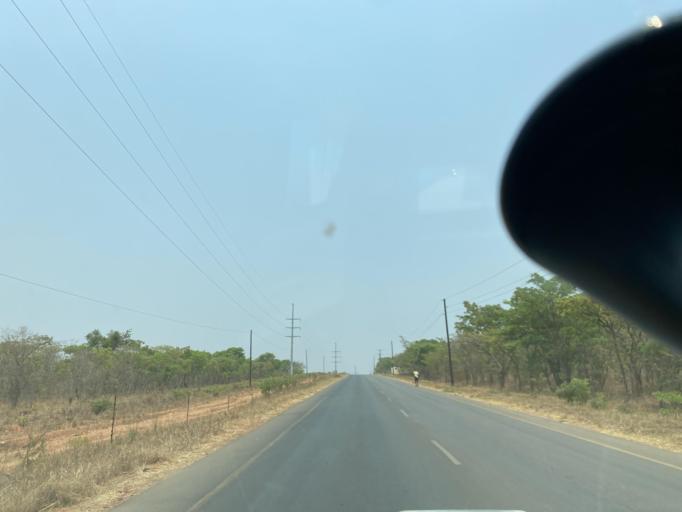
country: ZM
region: Lusaka
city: Lusaka
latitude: -15.5300
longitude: 28.4659
